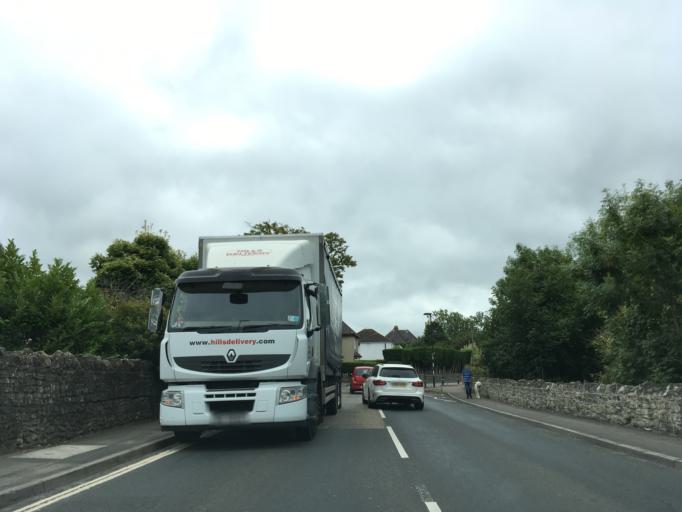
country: GB
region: England
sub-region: Bath and North East Somerset
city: Keynsham
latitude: 51.4106
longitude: -2.4931
